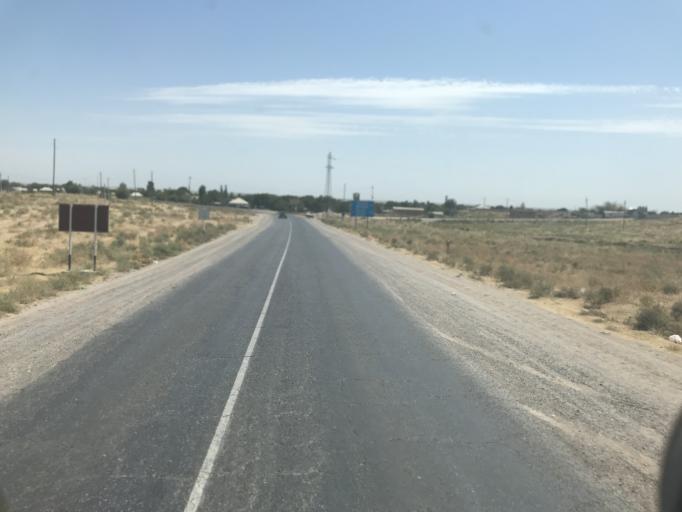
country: UZ
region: Toshkent
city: Yangiyul
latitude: 41.3293
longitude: 68.8912
